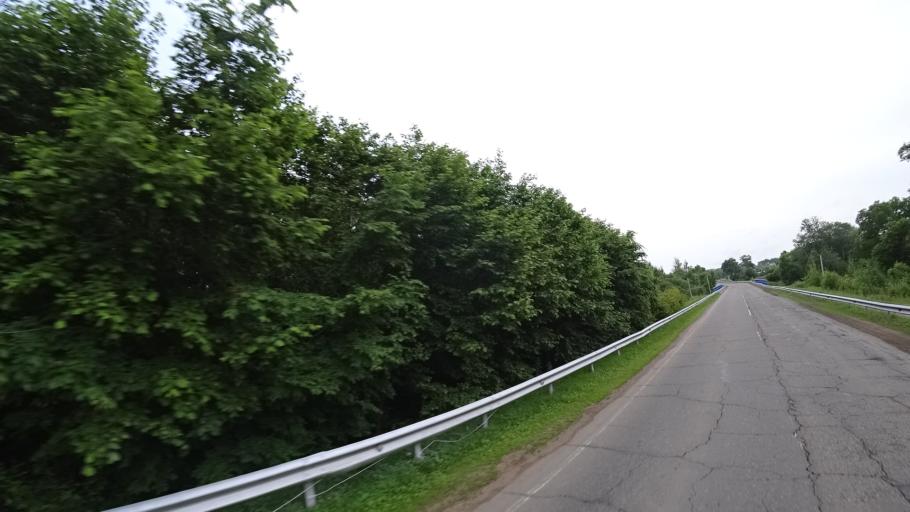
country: RU
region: Primorskiy
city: Novosysoyevka
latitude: 44.2327
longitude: 133.3759
